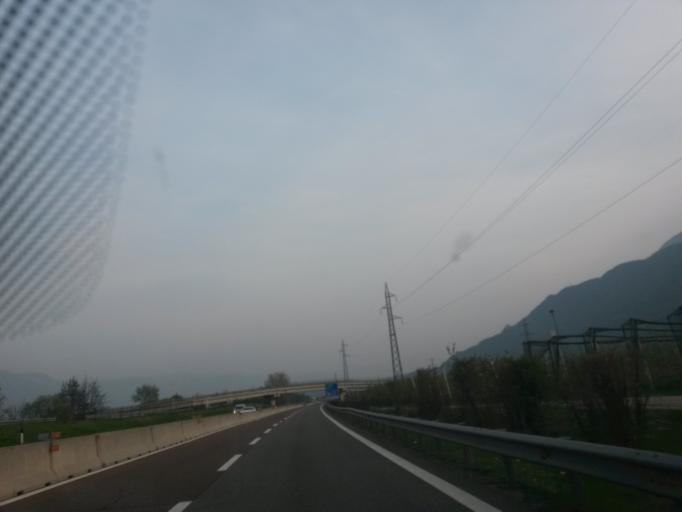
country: IT
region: Trentino-Alto Adige
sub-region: Bolzano
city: Terlano
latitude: 46.5315
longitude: 11.2393
